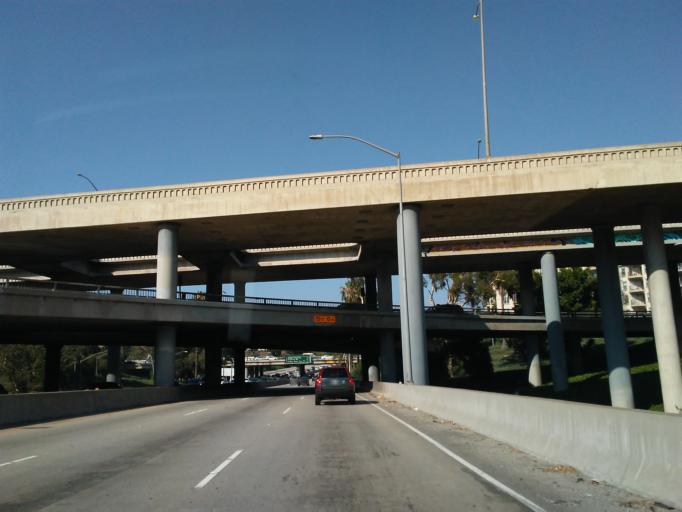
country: US
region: California
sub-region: Los Angeles County
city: Los Angeles
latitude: 34.0622
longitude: -118.2491
